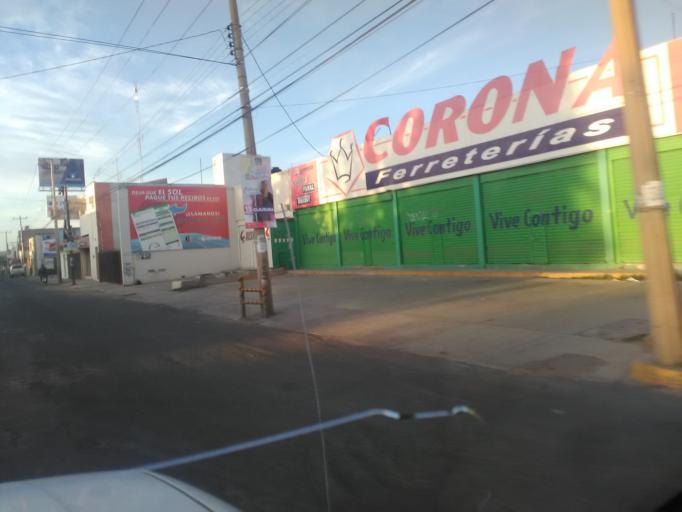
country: MX
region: Durango
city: Victoria de Durango
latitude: 24.0015
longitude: -104.6624
